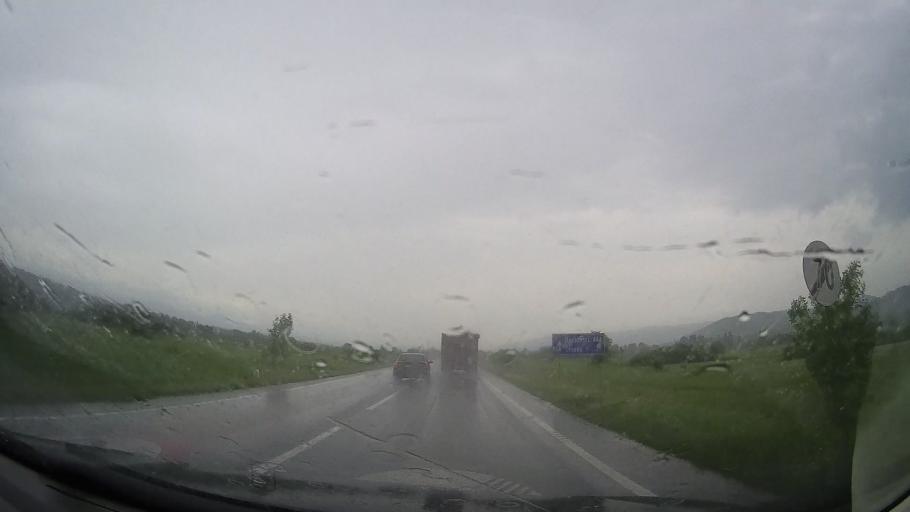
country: RO
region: Caras-Severin
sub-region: Comuna Bucosnita
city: Petrosnita
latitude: 45.3312
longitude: 22.2684
